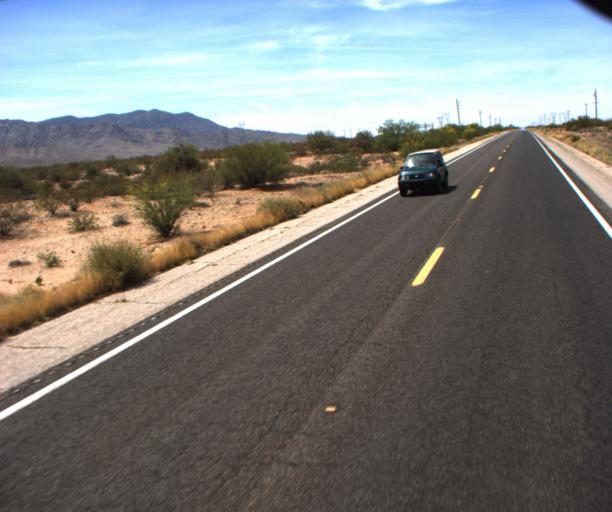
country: US
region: Arizona
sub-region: La Paz County
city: Salome
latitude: 33.9102
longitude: -113.2777
